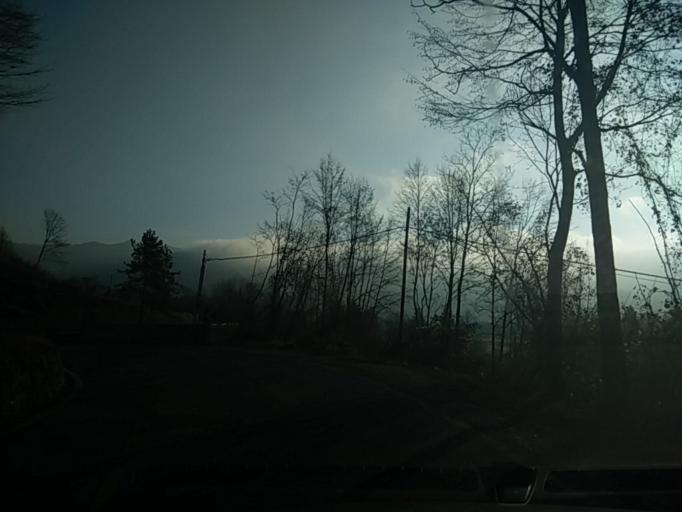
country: IT
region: Veneto
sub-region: Provincia di Belluno
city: Trichiana
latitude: 46.0467
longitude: 12.1565
